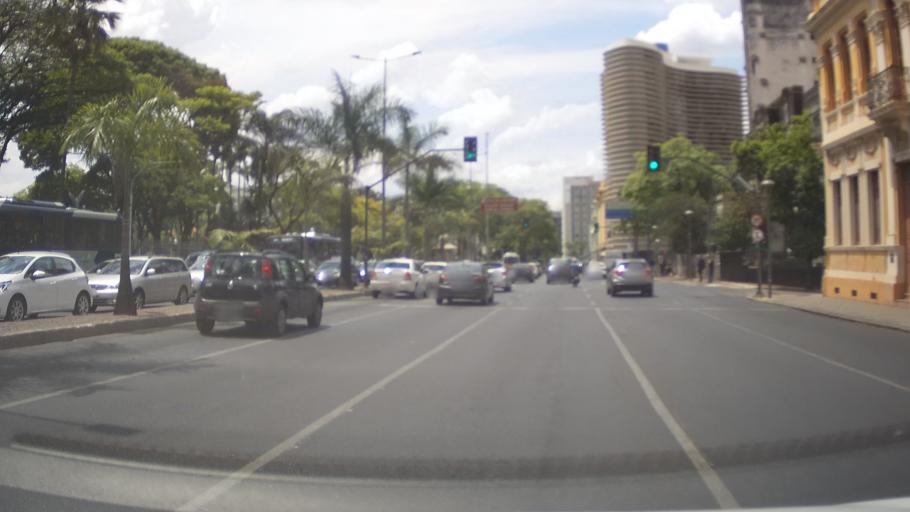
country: BR
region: Minas Gerais
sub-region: Belo Horizonte
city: Belo Horizonte
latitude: -19.9339
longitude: -43.9378
